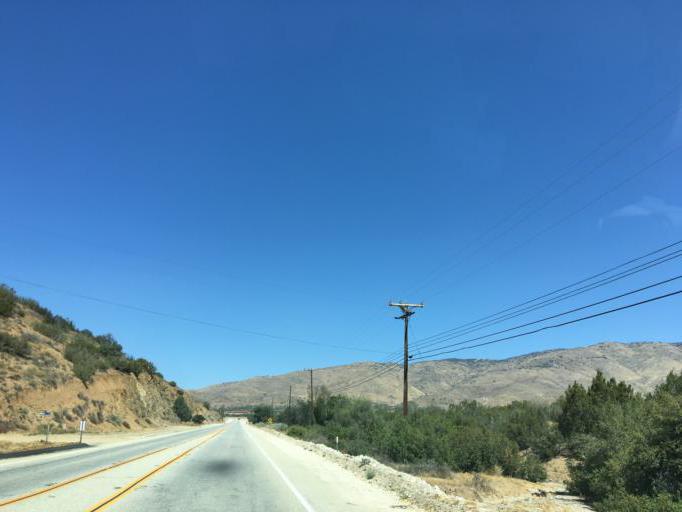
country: US
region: California
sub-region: Los Angeles County
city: Acton
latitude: 34.5115
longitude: -118.2356
